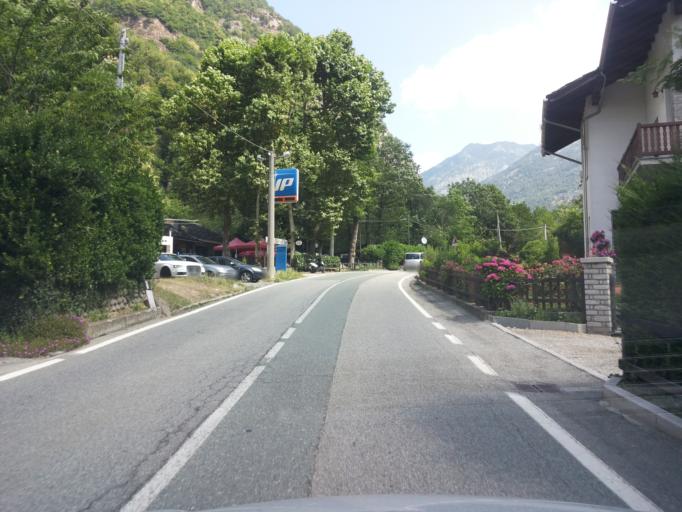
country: IT
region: Aosta Valley
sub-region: Valle d'Aosta
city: Lillianes
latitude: 45.6363
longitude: 7.8486
